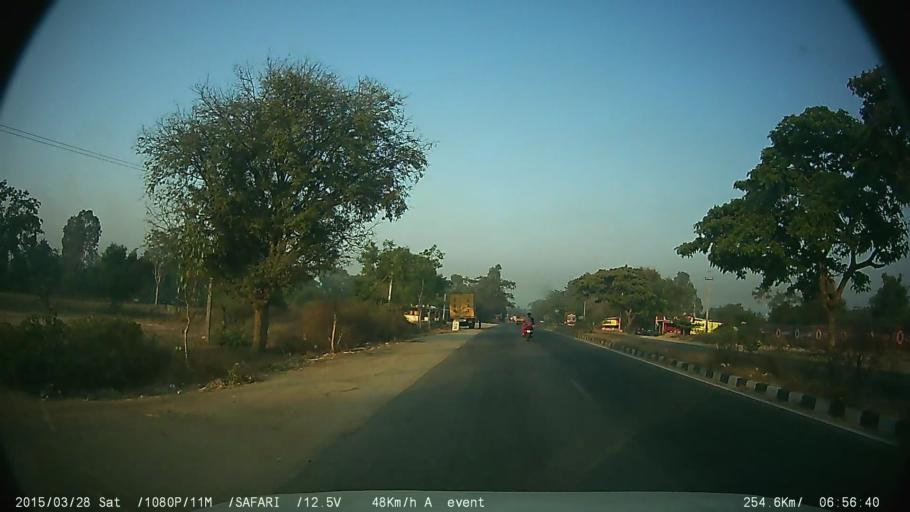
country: IN
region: Karnataka
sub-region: Mandya
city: Maddur
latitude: 12.5716
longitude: 77.0106
